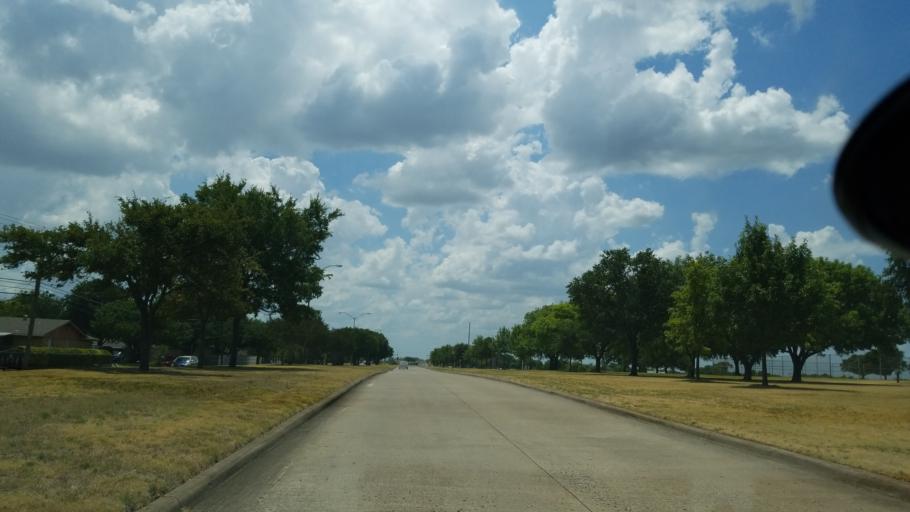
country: US
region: Texas
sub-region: Dallas County
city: Cockrell Hill
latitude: 32.7245
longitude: -96.9003
